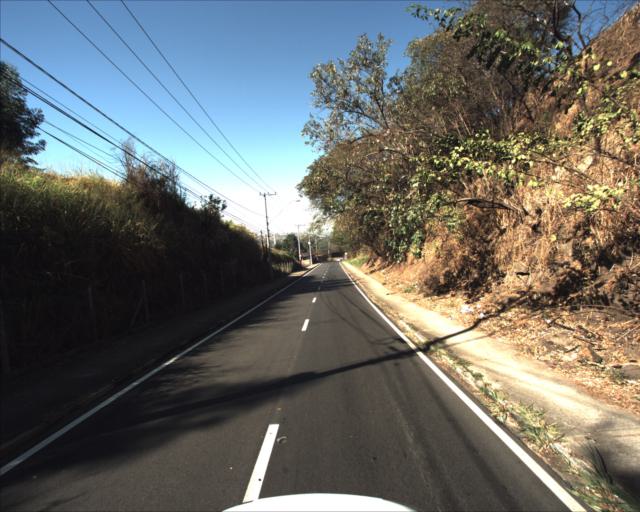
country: BR
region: Sao Paulo
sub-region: Sorocaba
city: Sorocaba
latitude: -23.5169
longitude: -47.4535
